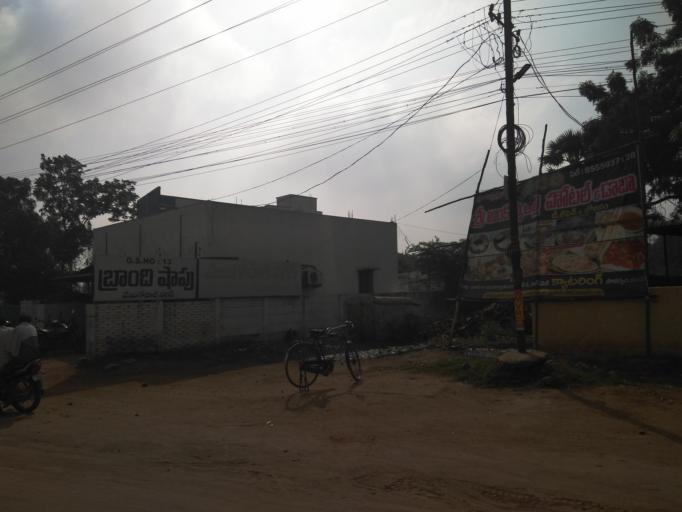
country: IN
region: Andhra Pradesh
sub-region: Nellore
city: Nellore
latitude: 14.4649
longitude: 80.0072
